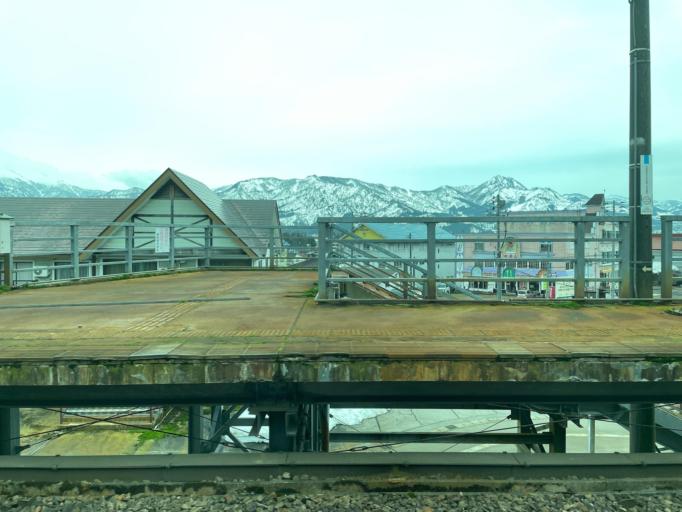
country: JP
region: Niigata
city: Shiozawa
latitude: 37.0288
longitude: 138.8281
